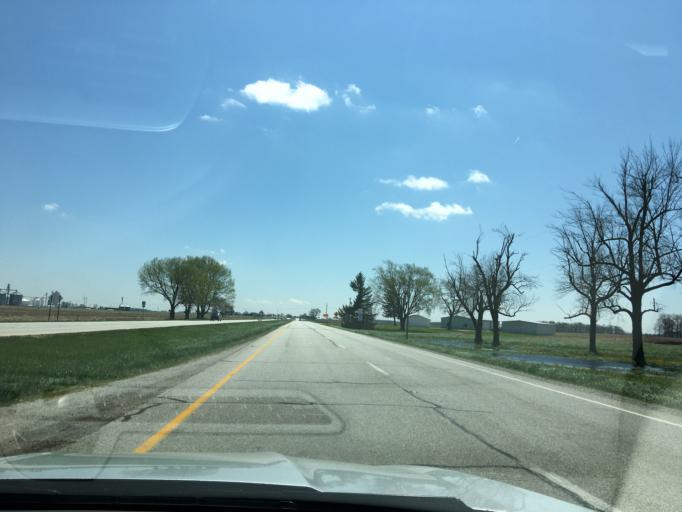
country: US
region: Indiana
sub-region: Clinton County
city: Mulberry
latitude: 40.2521
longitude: -86.6989
